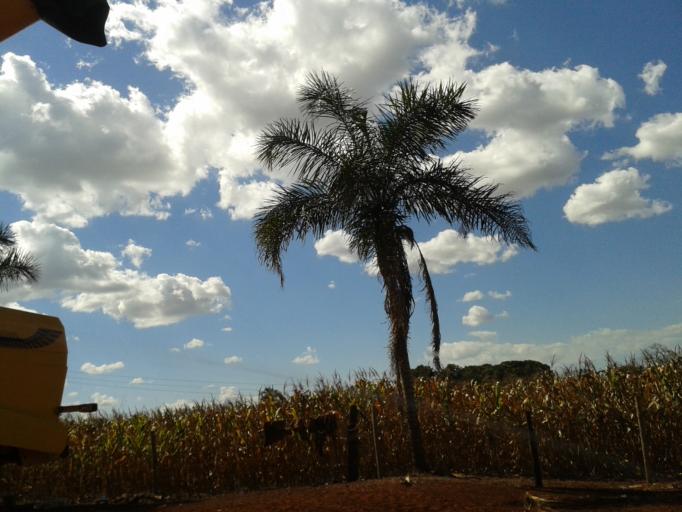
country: BR
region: Minas Gerais
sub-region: Capinopolis
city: Capinopolis
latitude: -18.6282
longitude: -49.4768
